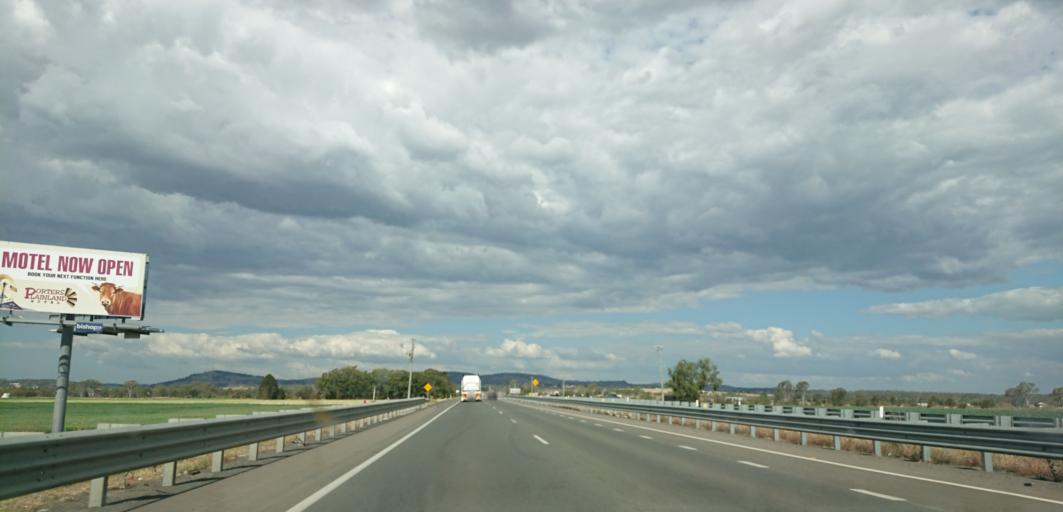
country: AU
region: Queensland
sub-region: Lockyer Valley
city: Gatton
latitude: -27.5464
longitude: 152.3818
